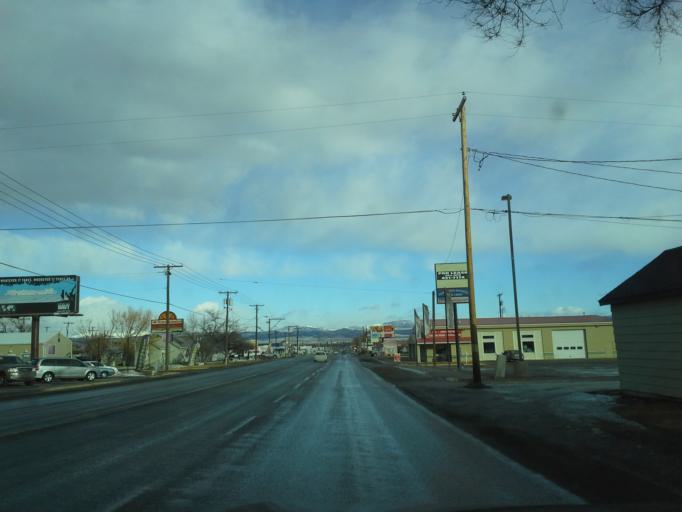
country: US
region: Montana
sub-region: Lewis and Clark County
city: Helena
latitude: 46.6031
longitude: -112.0206
